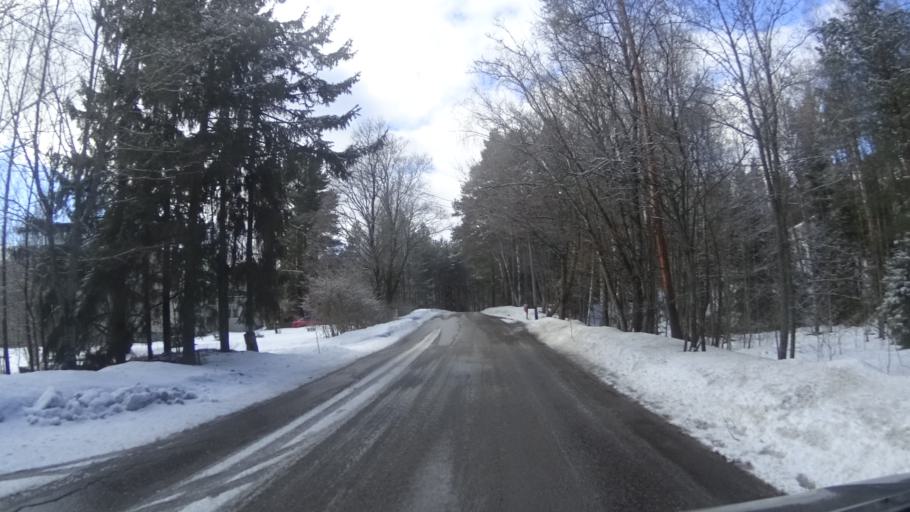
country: FI
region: Uusimaa
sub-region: Helsinki
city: Vantaa
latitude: 60.2528
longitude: 25.1678
